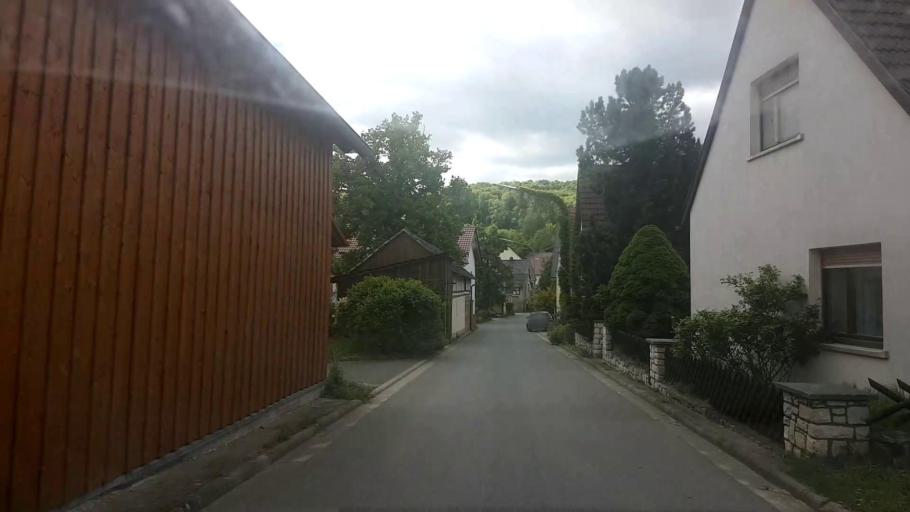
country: DE
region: Bavaria
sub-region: Upper Franconia
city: Bad Staffelstein
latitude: 50.1020
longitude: 11.0333
